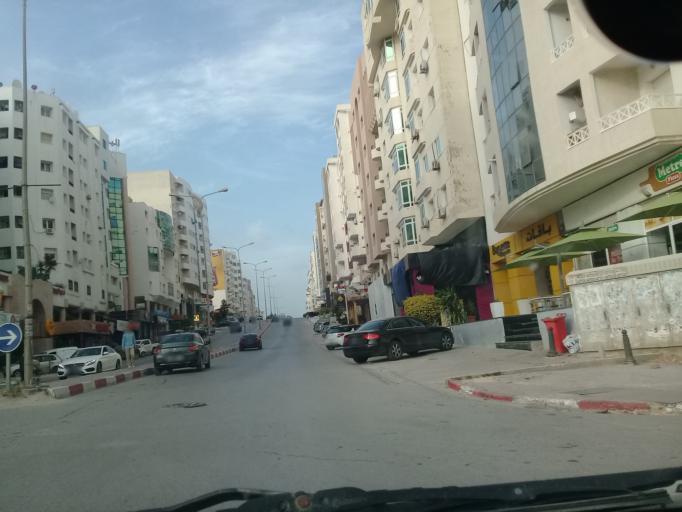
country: TN
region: Ariana
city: Ariana
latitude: 36.8612
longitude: 10.1639
